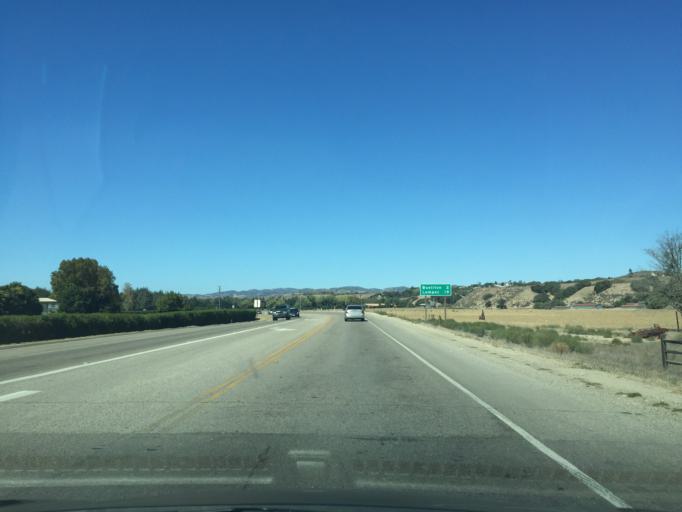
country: US
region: California
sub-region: Santa Barbara County
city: Solvang
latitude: 34.5960
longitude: -120.1545
